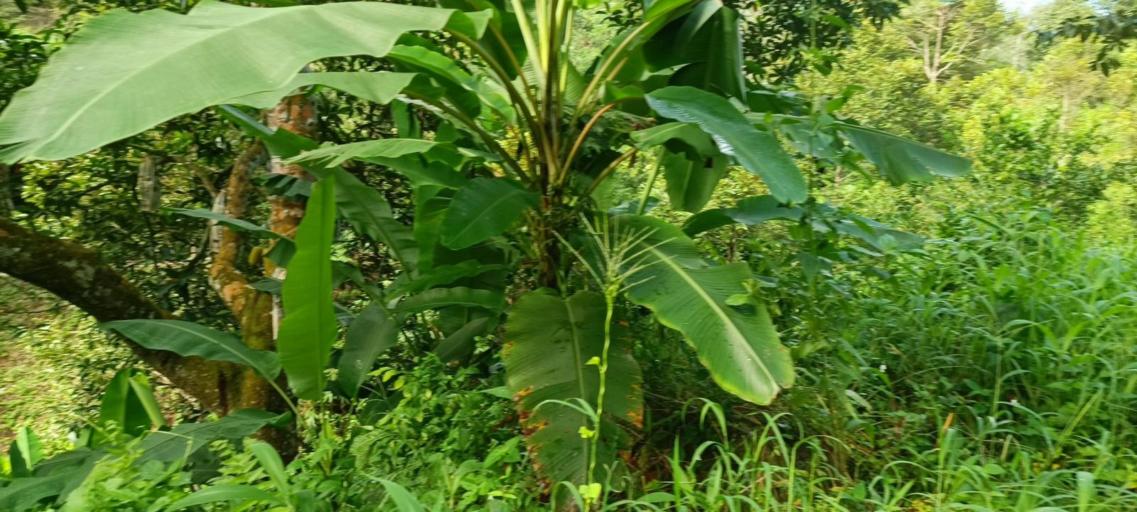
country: MY
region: Penang
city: Kampung Sungai Ara
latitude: 5.3205
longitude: 100.2428
